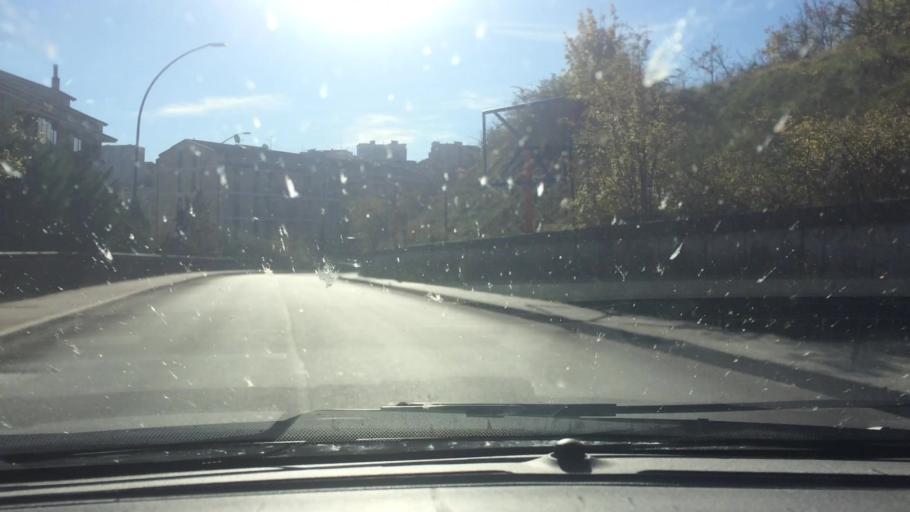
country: IT
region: Basilicate
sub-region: Provincia di Potenza
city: Potenza
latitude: 40.6430
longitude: 15.7964
